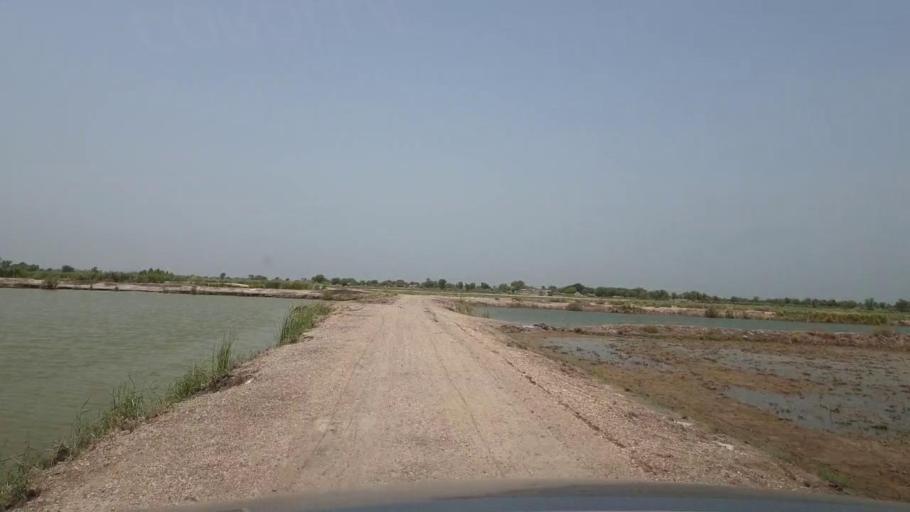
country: PK
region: Sindh
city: Madeji
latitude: 27.7631
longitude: 68.3855
